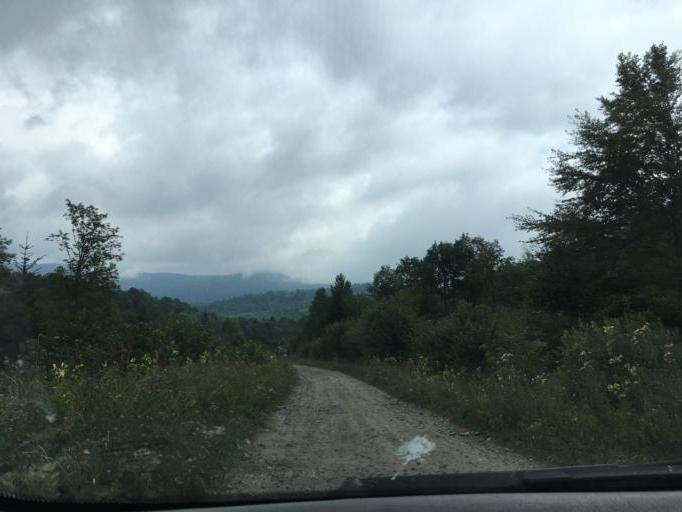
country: PL
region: Subcarpathian Voivodeship
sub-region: Powiat bieszczadzki
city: Lutowiska
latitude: 49.1911
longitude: 22.6137
